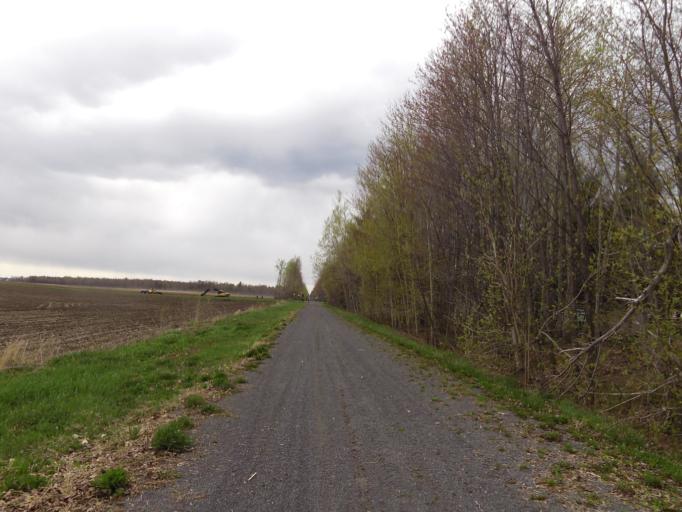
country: CA
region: Ontario
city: Bourget
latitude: 45.4824
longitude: -75.0366
